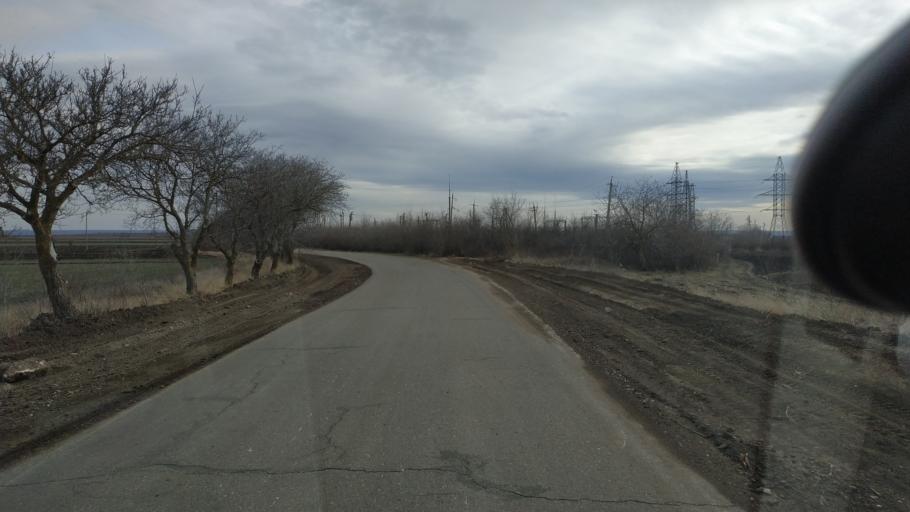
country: MD
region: Telenesti
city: Cocieri
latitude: 47.2896
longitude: 29.0802
